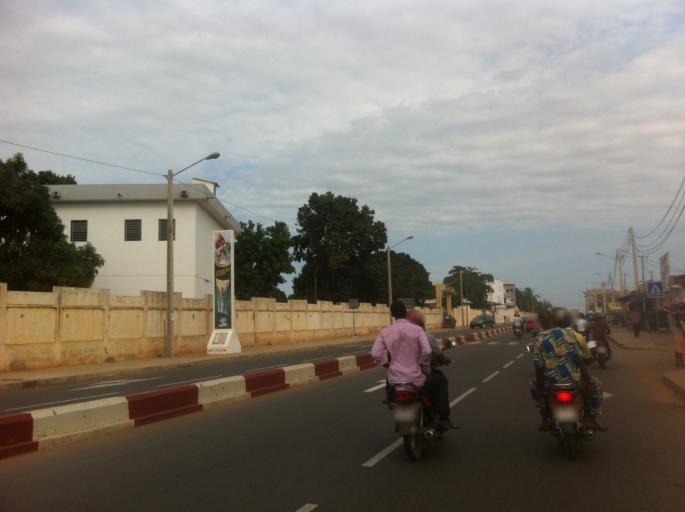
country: TG
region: Maritime
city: Lome
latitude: 6.1454
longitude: 1.2048
